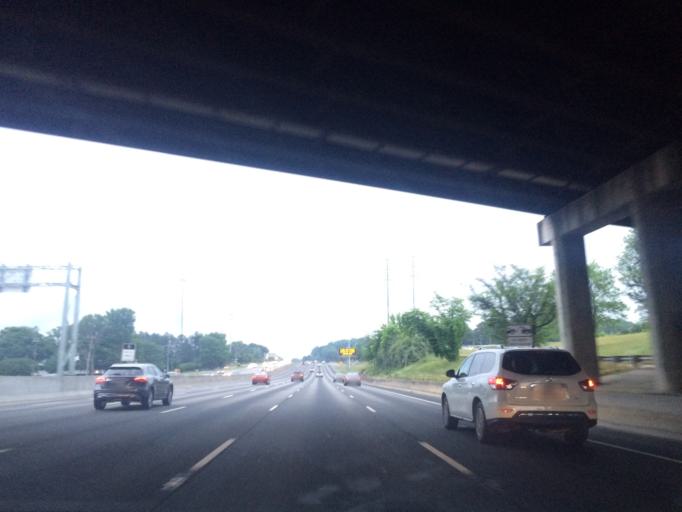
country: US
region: Georgia
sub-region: DeKalb County
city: North Druid Hills
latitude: 33.8319
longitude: -84.3355
